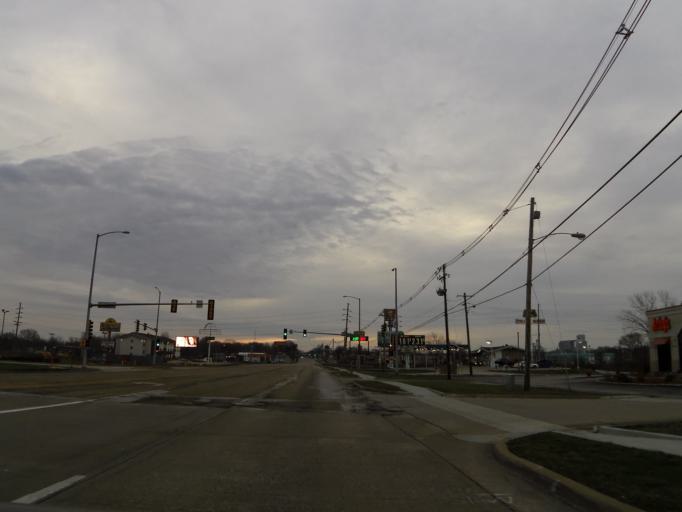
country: US
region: Illinois
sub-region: McLean County
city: Bloomington
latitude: 40.4838
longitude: -89.0217
